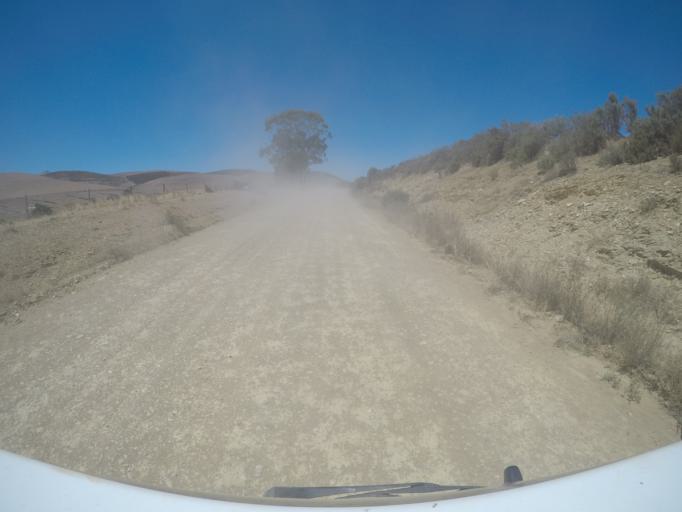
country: ZA
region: Western Cape
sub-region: Overberg District Municipality
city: Grabouw
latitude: -34.1008
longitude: 19.2047
